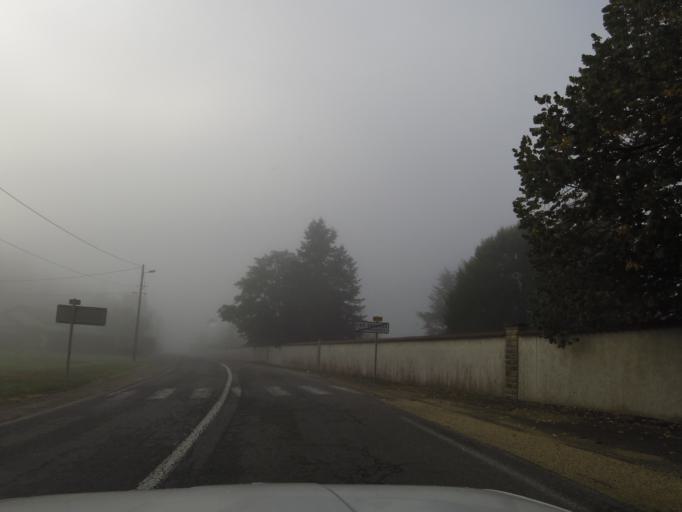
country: FR
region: Rhone-Alpes
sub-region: Departement de l'Isere
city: Bouvesse-Quirieu
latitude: 45.7928
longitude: 5.4610
